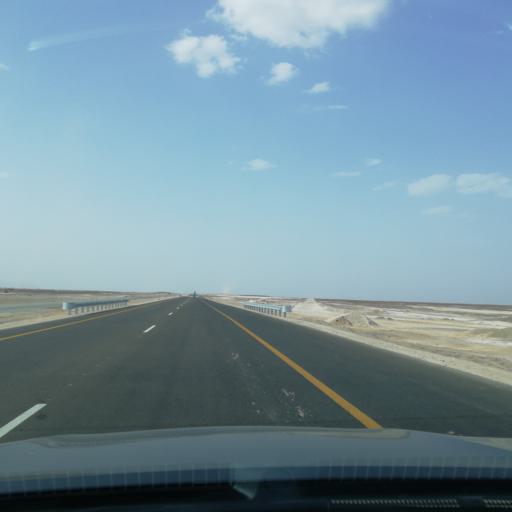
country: OM
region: Muhafazat ad Dakhiliyah
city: Adam
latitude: 22.0464
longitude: 57.5110
